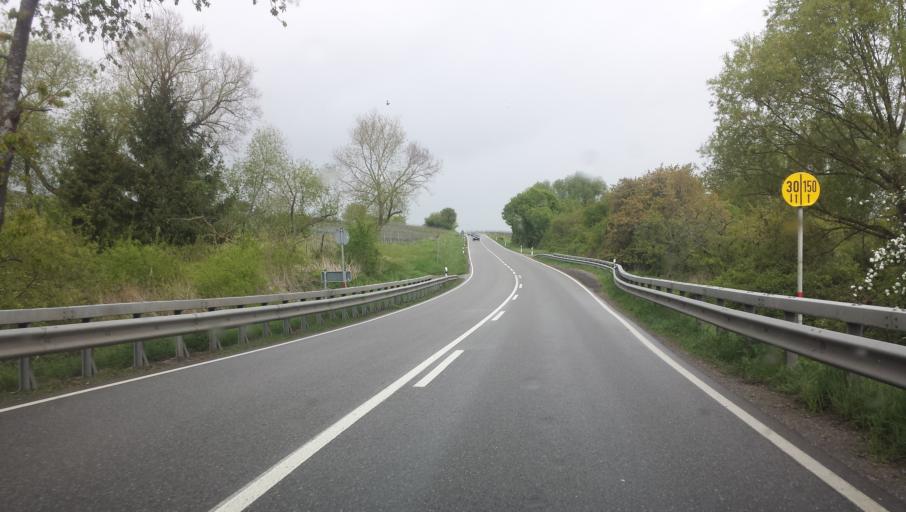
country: DE
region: Rheinland-Pfalz
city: Oberotterbach
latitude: 49.0763
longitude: 7.9713
